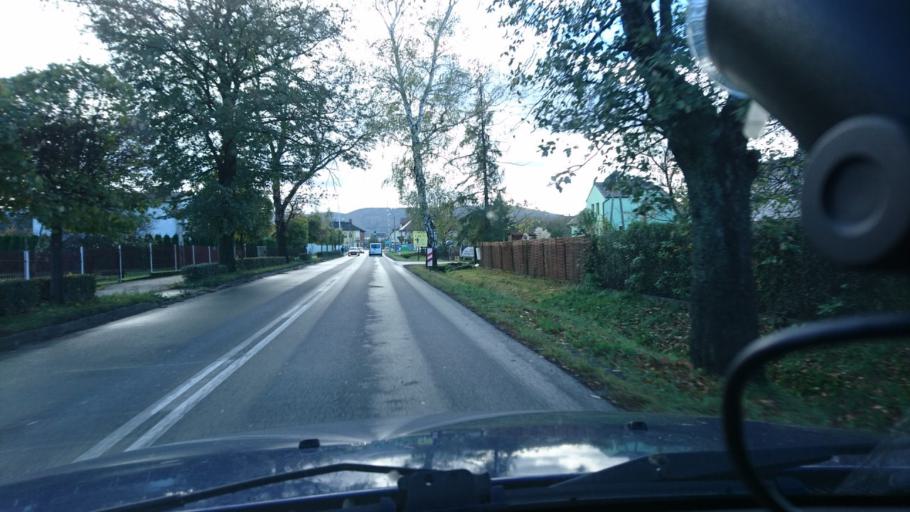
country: PL
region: Silesian Voivodeship
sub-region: Powiat bielski
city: Jasienica
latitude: 49.8071
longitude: 18.9213
